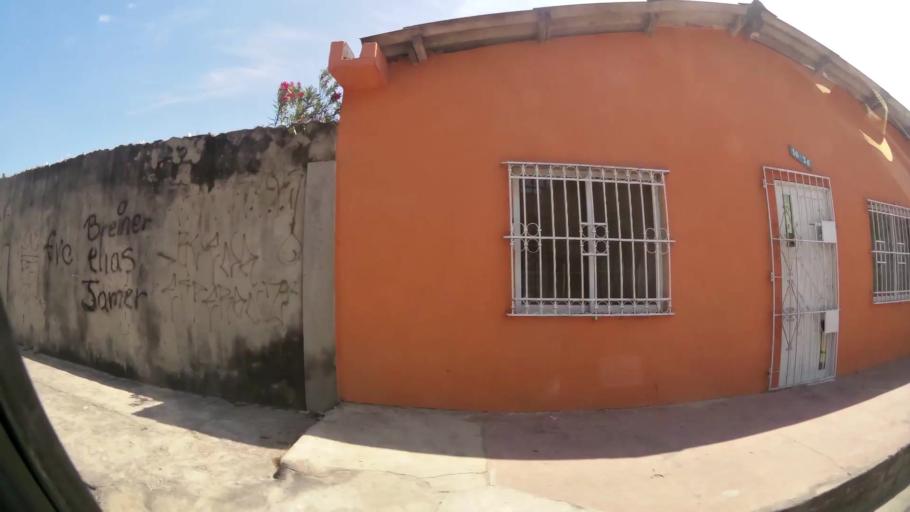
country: CO
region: Atlantico
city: Barranquilla
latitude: 10.9645
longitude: -74.8069
